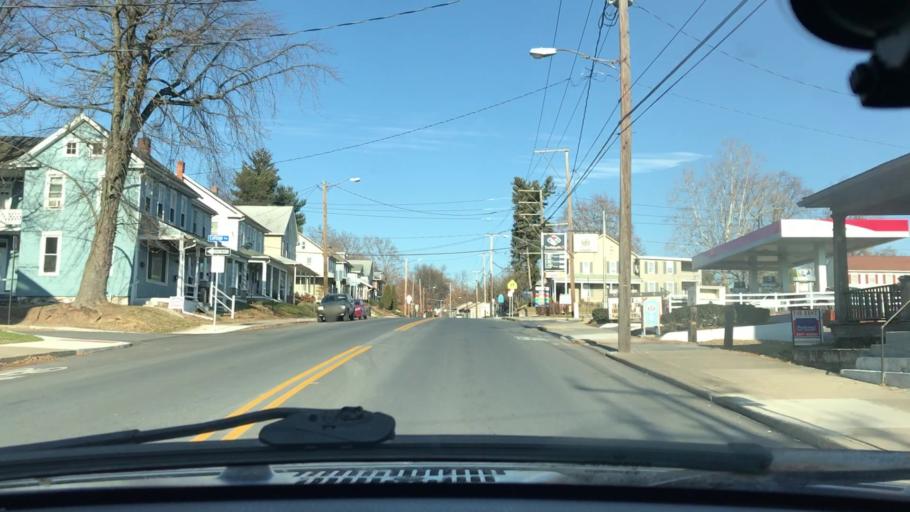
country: US
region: Pennsylvania
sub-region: Lancaster County
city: Elizabethtown
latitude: 40.1549
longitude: -76.6081
